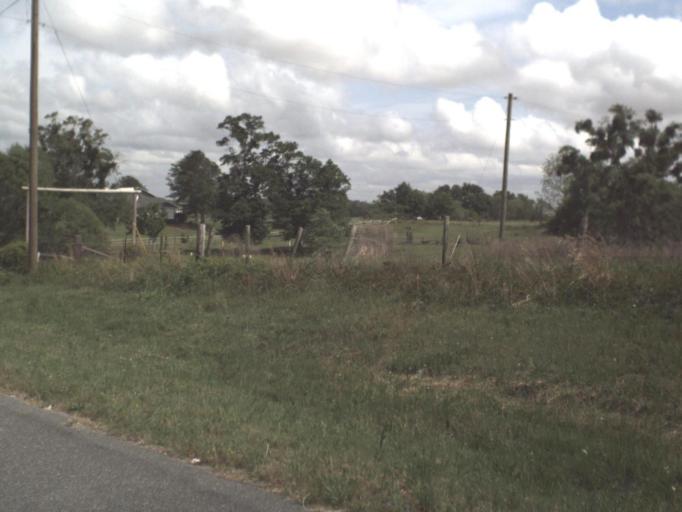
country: US
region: Florida
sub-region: Santa Rosa County
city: Point Baker
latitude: 30.8068
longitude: -87.1173
